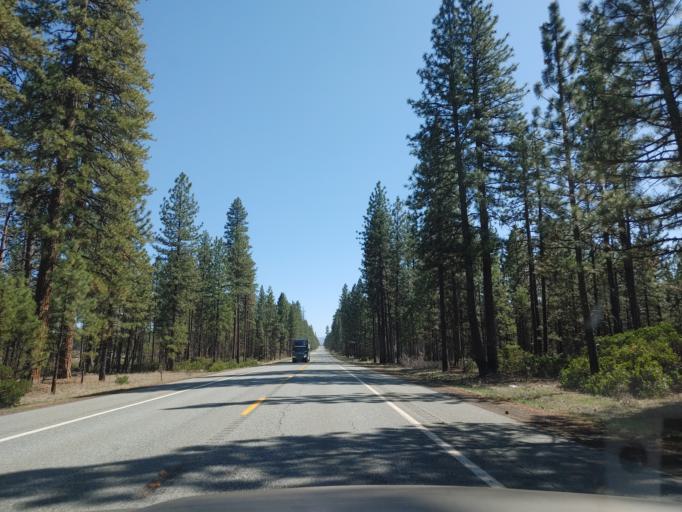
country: US
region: California
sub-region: Shasta County
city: Burney
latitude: 40.9850
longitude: -121.6249
